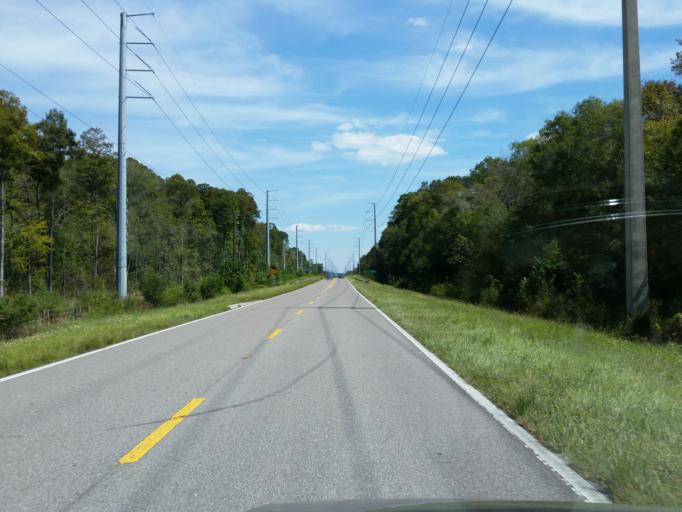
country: US
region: Florida
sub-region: Pasco County
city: Zephyrhills North
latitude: 28.2593
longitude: -82.1085
